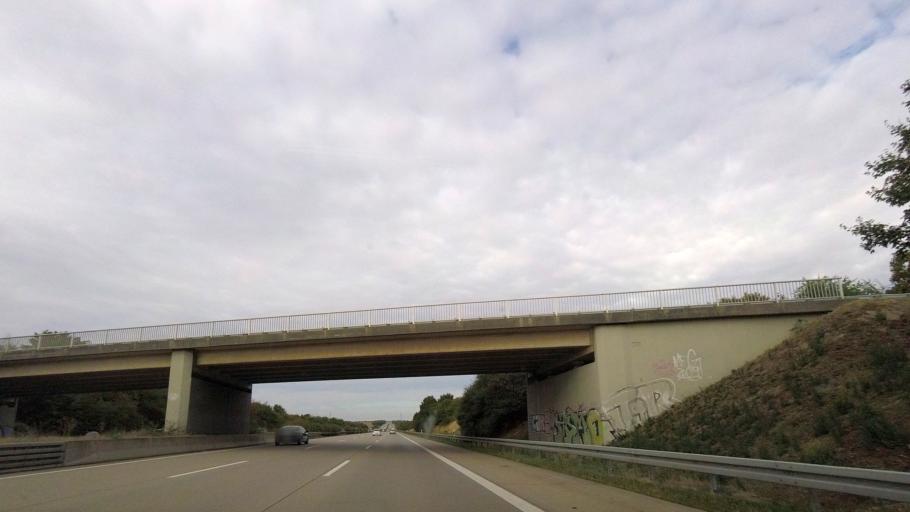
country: DE
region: Thuringia
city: Eisenberg
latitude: 50.9976
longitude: 11.9173
